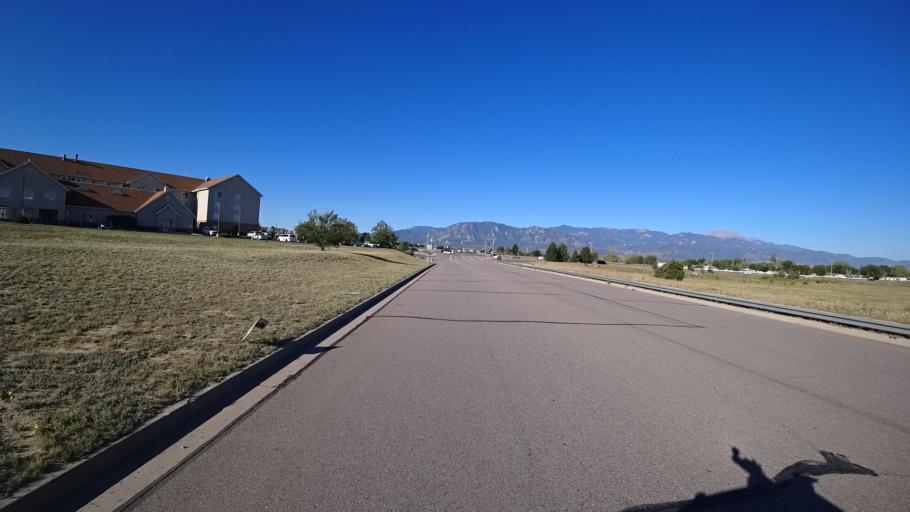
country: US
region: Colorado
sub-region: El Paso County
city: Security-Widefield
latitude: 38.7898
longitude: -104.7272
